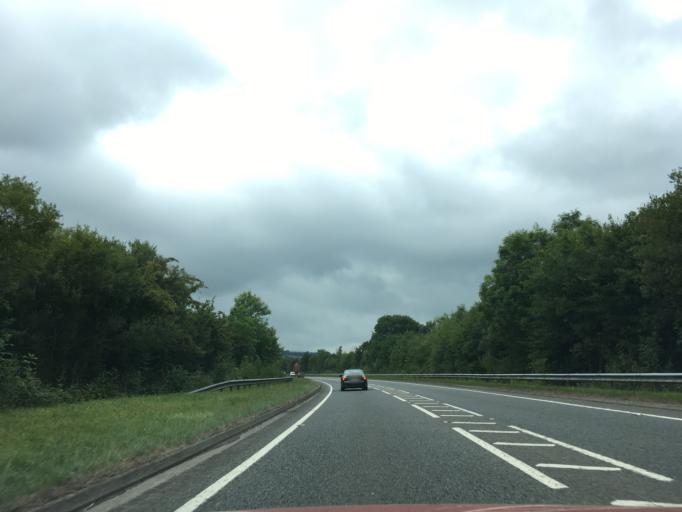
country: GB
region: Wales
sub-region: Carmarthenshire
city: Whitland
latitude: 51.8242
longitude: -4.6217
